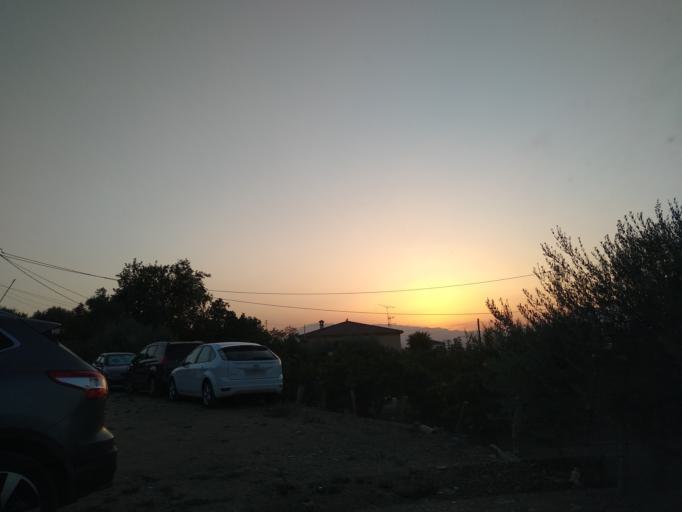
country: ES
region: Andalusia
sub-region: Provincia de Malaga
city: Alhaurin el Grande
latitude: 36.6532
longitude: -4.6753
